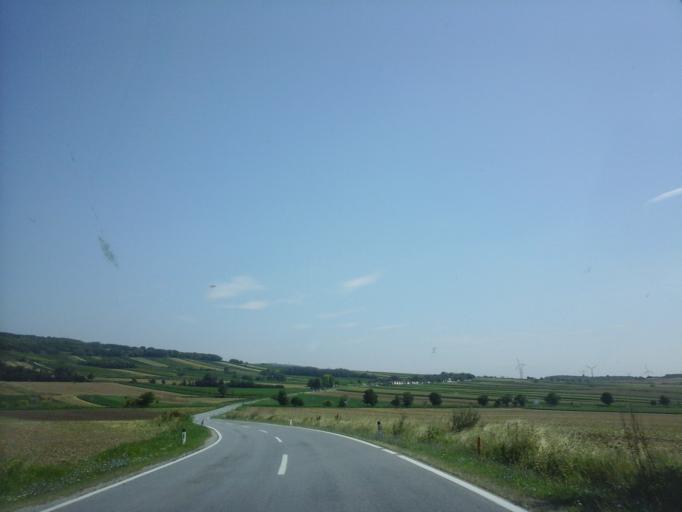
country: AT
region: Burgenland
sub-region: Politischer Bezirk Neusiedl am See
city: Edelstal
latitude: 48.0819
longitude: 16.9684
